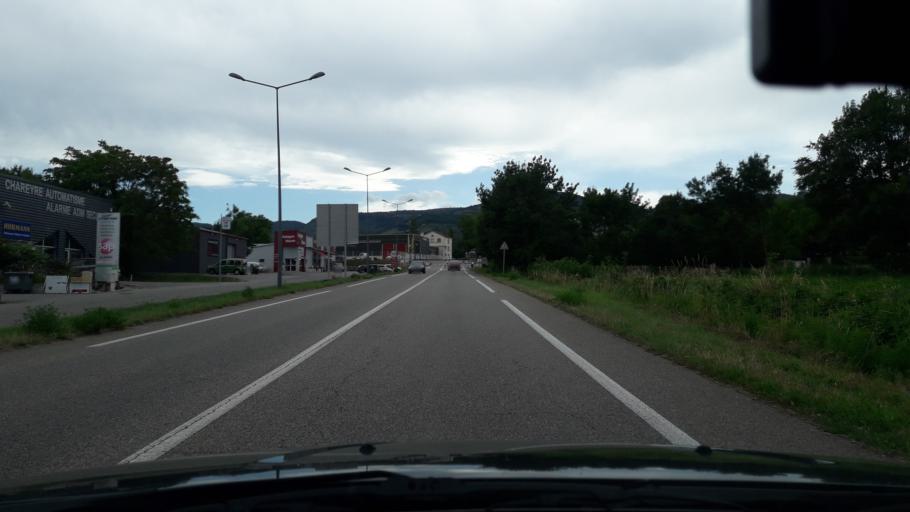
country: FR
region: Rhone-Alpes
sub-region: Departement de l'Ardeche
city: Chomerac
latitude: 44.7073
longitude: 4.6652
